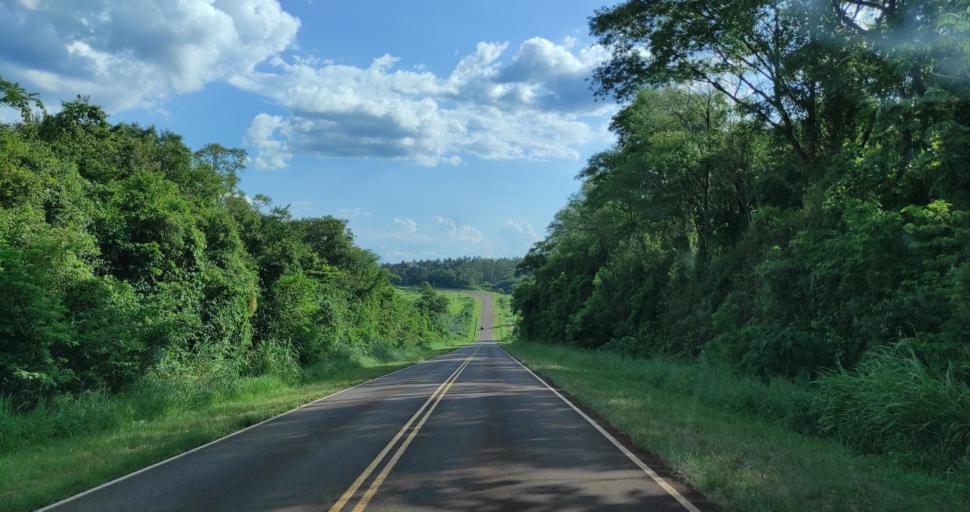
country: AR
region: Misiones
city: San Vicente
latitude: -26.3549
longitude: -54.2122
